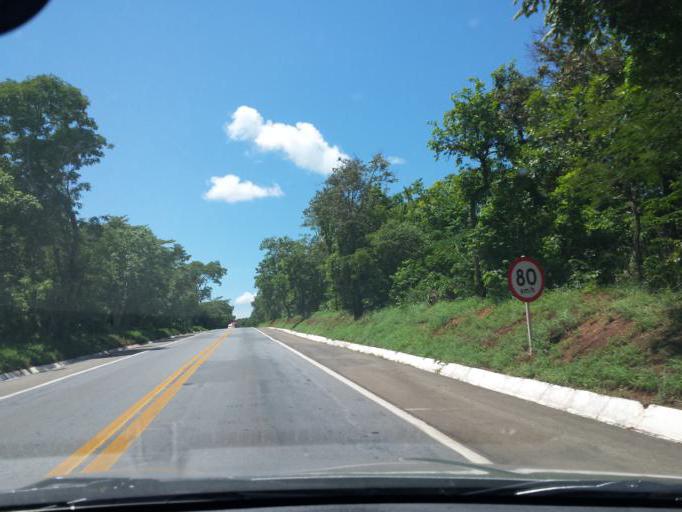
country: BR
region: Goias
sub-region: Luziania
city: Luziania
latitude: -16.3955
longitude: -47.8246
